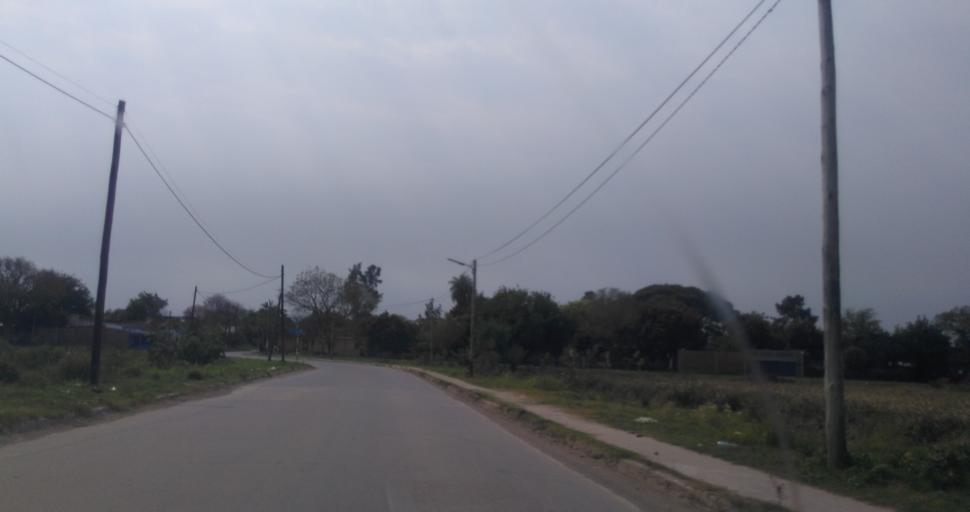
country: AR
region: Chaco
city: Fontana
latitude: -27.4201
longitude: -59.0269
